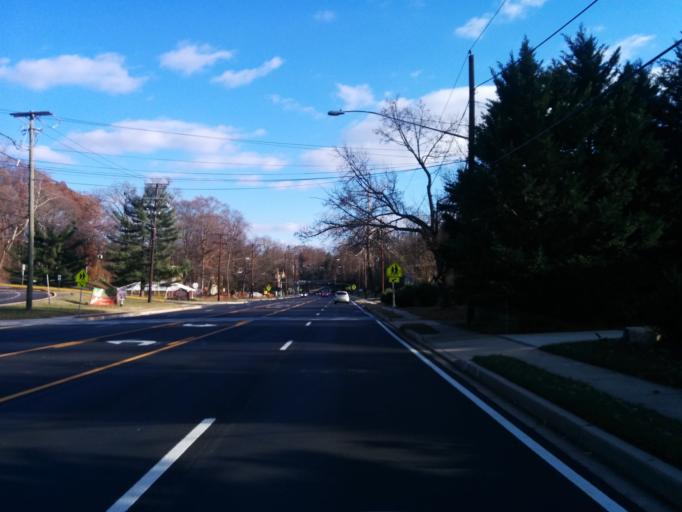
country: US
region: Maryland
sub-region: Montgomery County
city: Somerset
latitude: 38.9595
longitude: -77.1126
